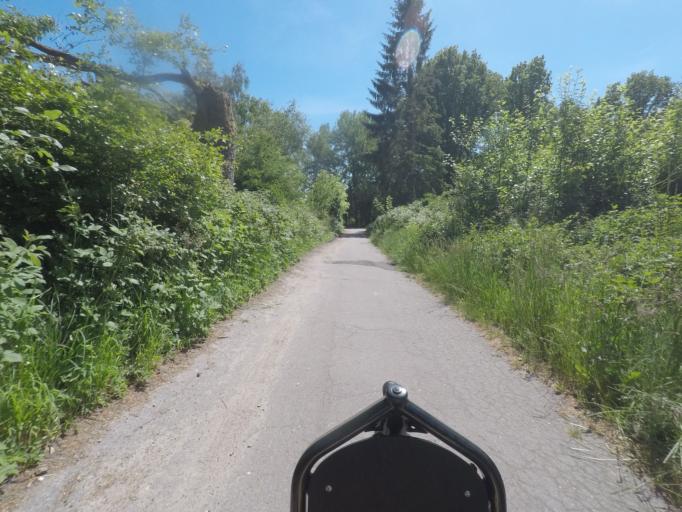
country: DE
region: Schleswig-Holstein
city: Stapelfeld
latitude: 53.6324
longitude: 10.2052
